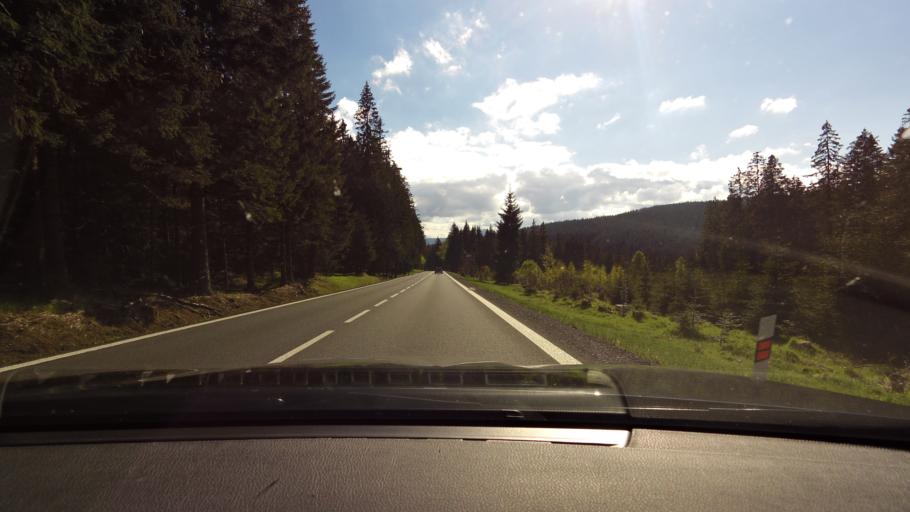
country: CZ
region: Plzensky
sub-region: Okres Klatovy
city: Zelezna Ruda
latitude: 49.1607
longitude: 13.2686
